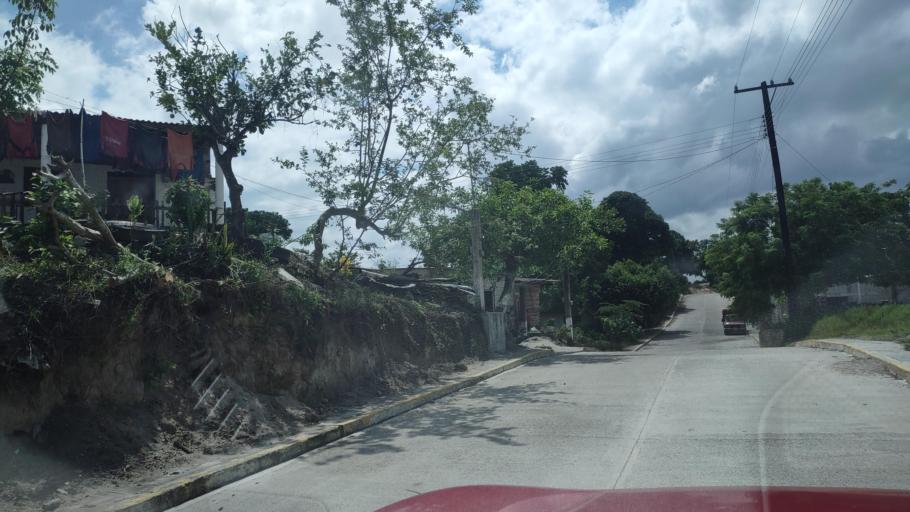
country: MX
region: Puebla
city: San Jose Acateno
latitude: 20.2175
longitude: -97.1343
